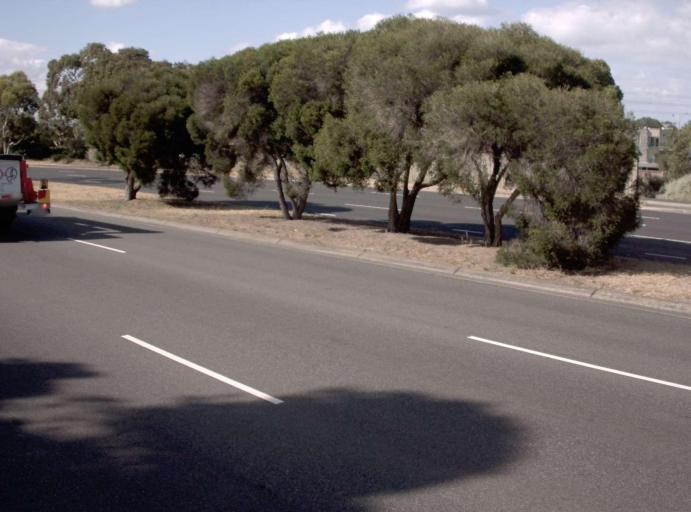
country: AU
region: Victoria
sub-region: Bayside
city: Moorabbin
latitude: -37.9314
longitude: 145.0330
